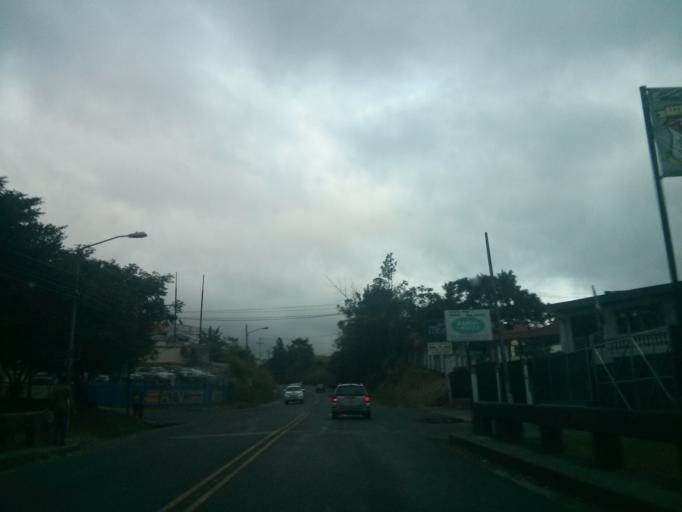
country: CR
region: San Jose
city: Curridabat
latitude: 9.9020
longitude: -84.0600
